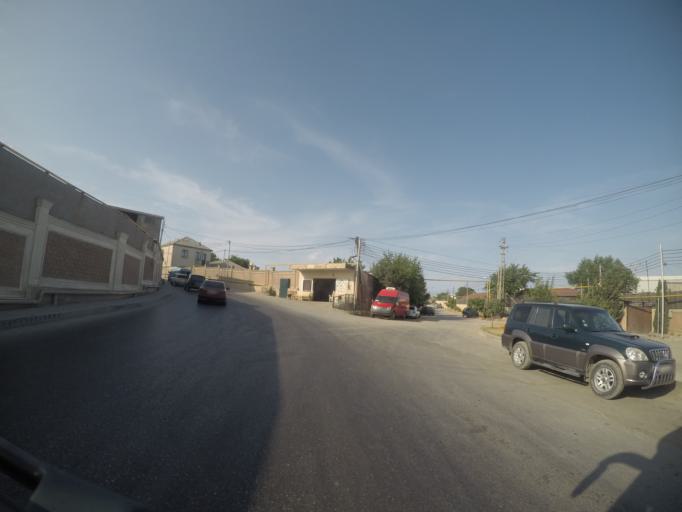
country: AZ
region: Baki
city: Binagadi
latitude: 40.4657
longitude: 49.8421
